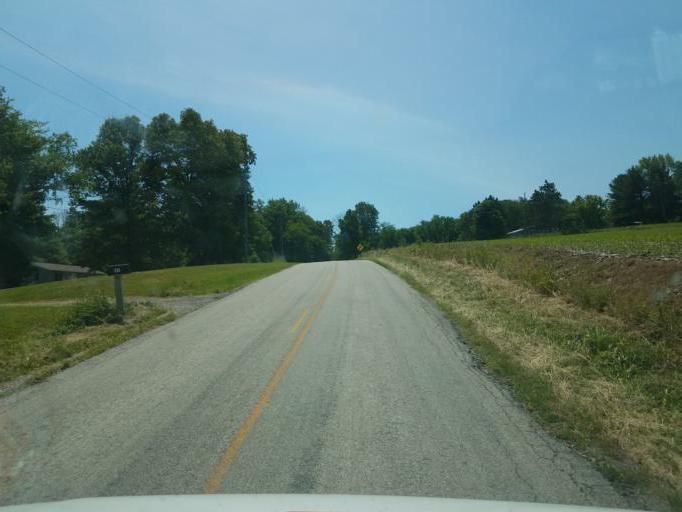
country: US
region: Ohio
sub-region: Ashland County
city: Loudonville
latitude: 40.5735
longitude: -82.3580
